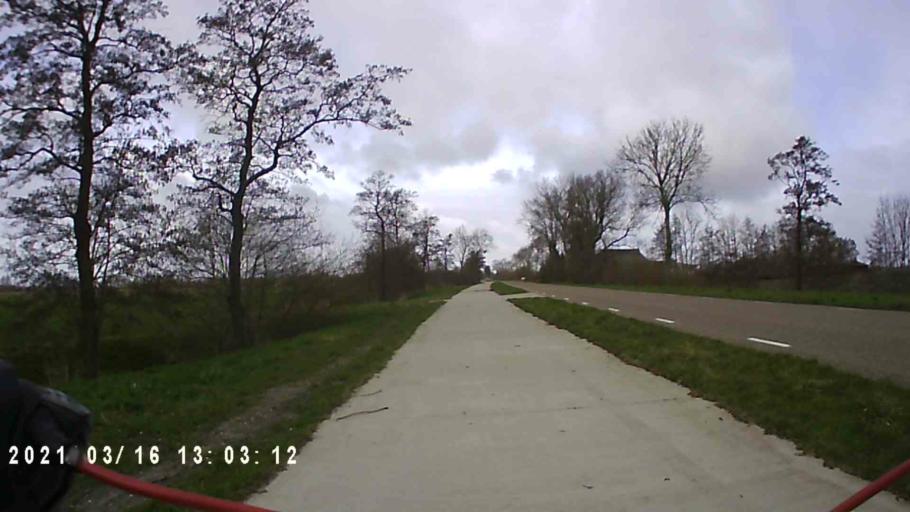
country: NL
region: Friesland
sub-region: Menameradiel
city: Berltsum
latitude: 53.2491
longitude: 5.6376
